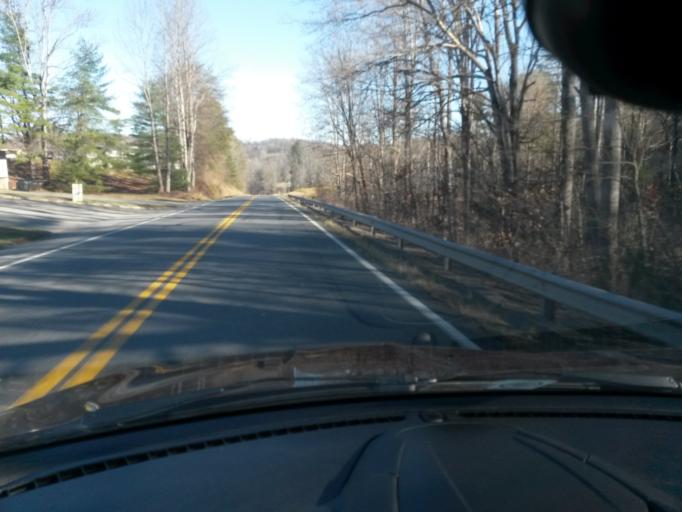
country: US
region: Virginia
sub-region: Patrick County
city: Patrick Springs
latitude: 36.7412
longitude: -80.2089
